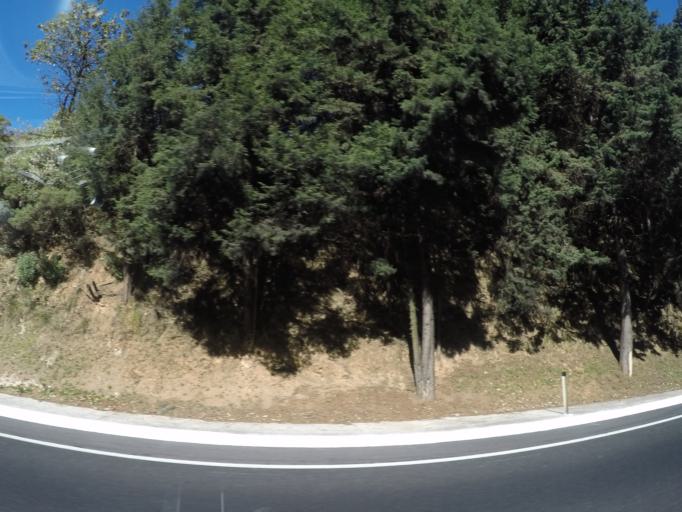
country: MX
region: Mexico City
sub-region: Cuajimalpa de Morelos
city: San Lorenzo Acopilco
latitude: 19.3178
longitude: -99.3278
